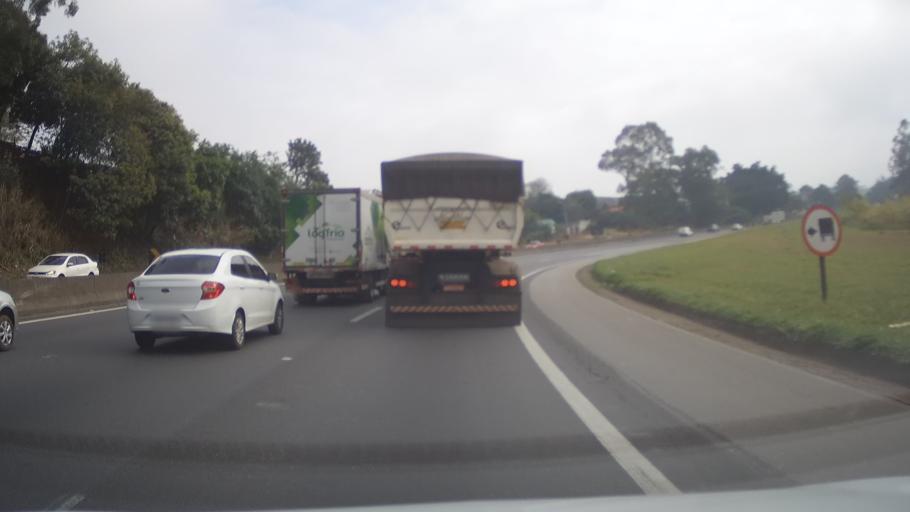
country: BR
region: Sao Paulo
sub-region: Atibaia
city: Atibaia
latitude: -23.0789
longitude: -46.5696
